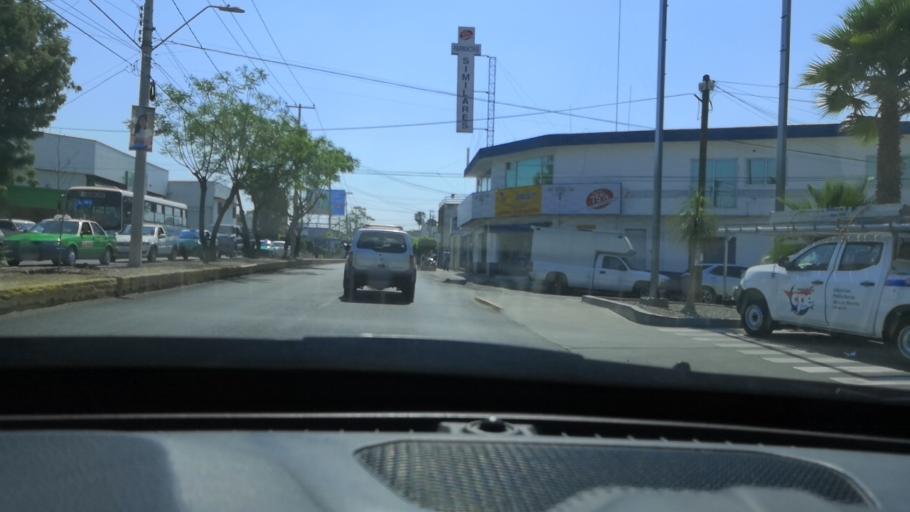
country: MX
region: Guanajuato
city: Leon
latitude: 21.1158
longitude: -101.6954
